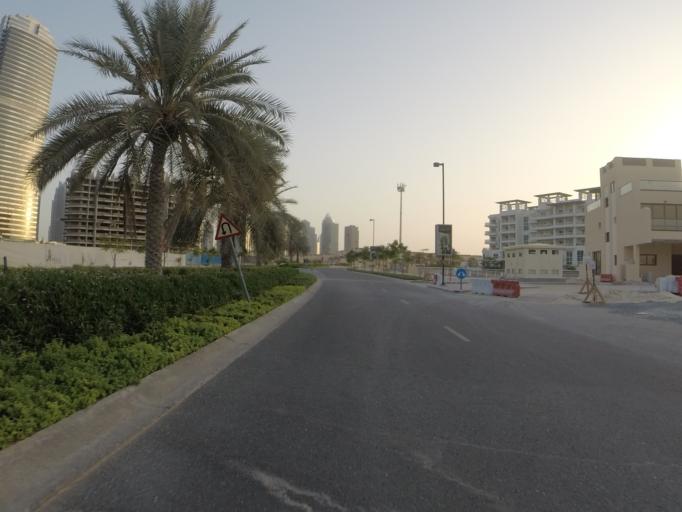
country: AE
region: Dubai
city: Dubai
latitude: 25.0659
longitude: 55.1466
